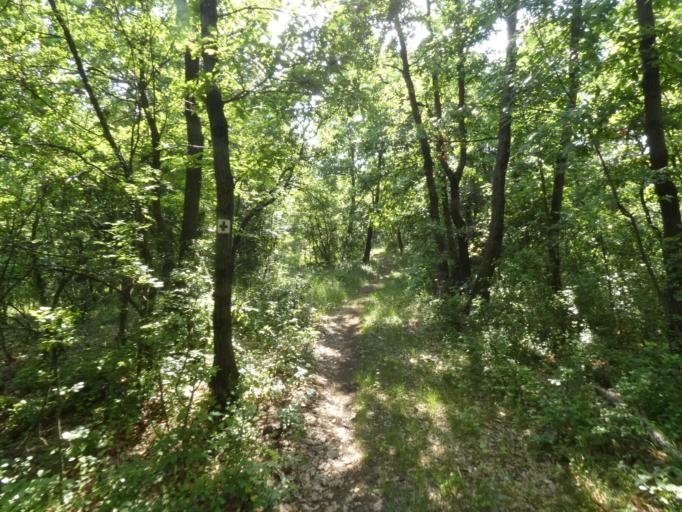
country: HU
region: Nograd
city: Szurdokpuspoki
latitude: 47.8558
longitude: 19.7202
